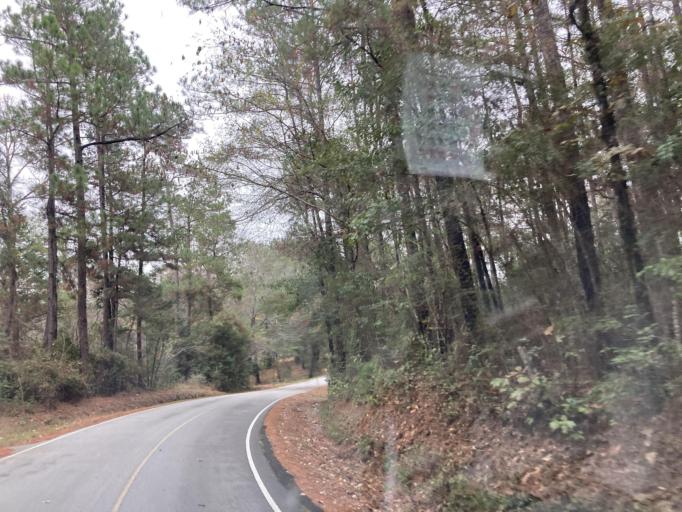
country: US
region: Mississippi
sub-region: Lamar County
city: Purvis
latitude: 31.2038
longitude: -89.4429
